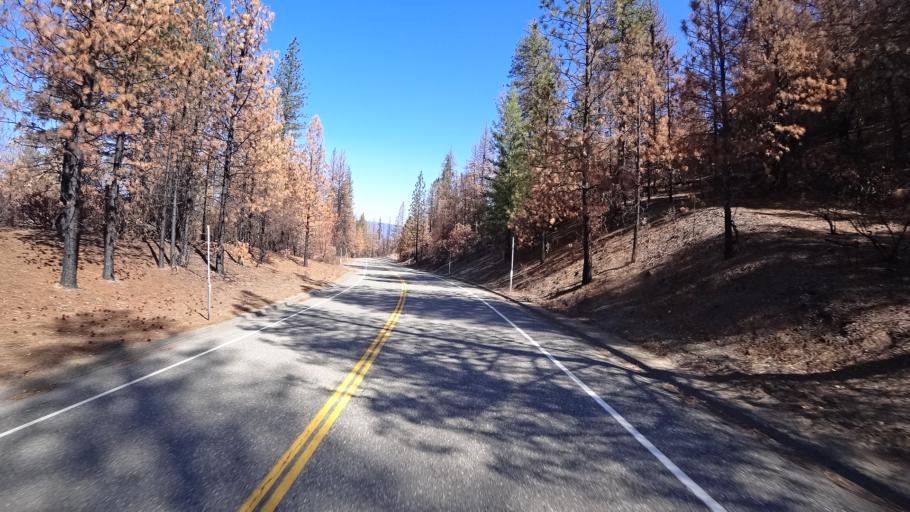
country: US
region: California
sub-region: Tehama County
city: Rancho Tehama Reserve
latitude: 39.6688
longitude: -122.7121
